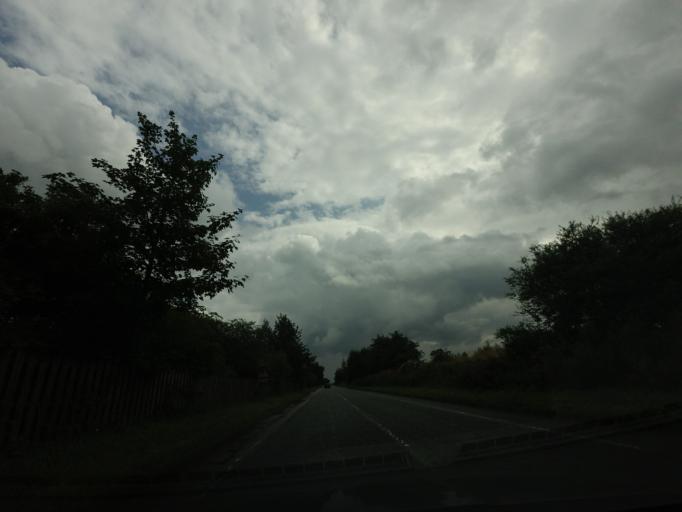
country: GB
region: Scotland
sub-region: Dumfries and Galloway
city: Lockerbie
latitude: 55.1161
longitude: -3.3593
